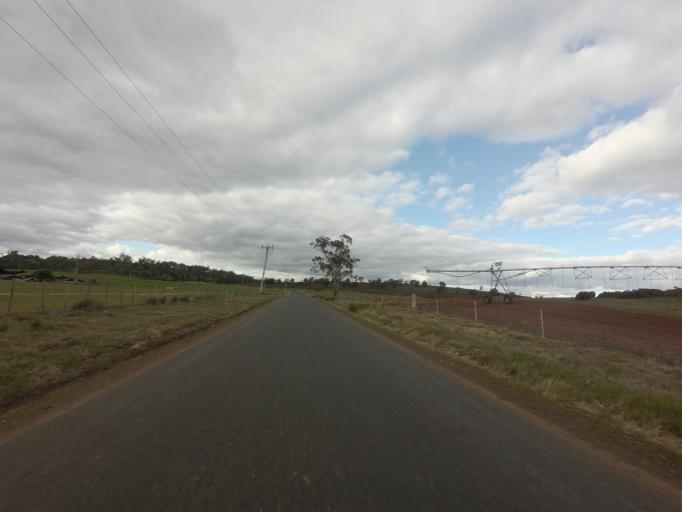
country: AU
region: Tasmania
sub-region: Northern Midlands
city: Evandale
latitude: -41.9001
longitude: 147.4040
